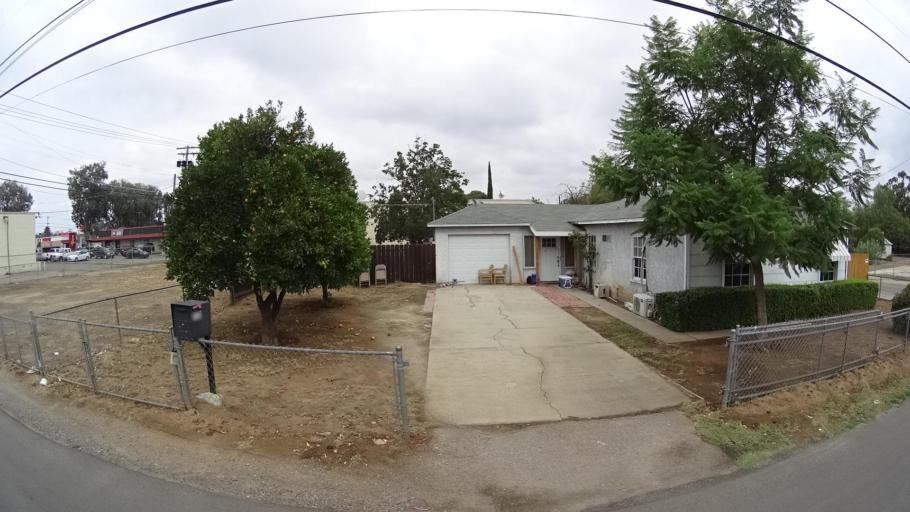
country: US
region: California
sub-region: San Diego County
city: Ramona
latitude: 33.0404
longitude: -116.8697
